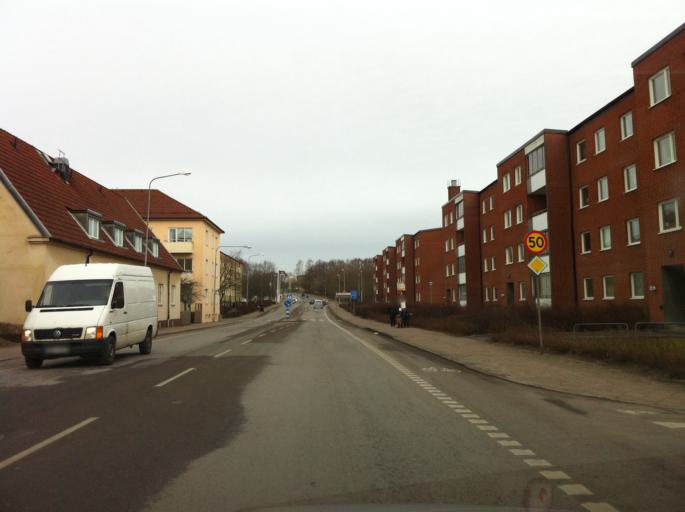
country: SE
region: Skane
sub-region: Angelholms Kommun
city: AEngelholm
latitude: 56.2462
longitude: 12.8728
